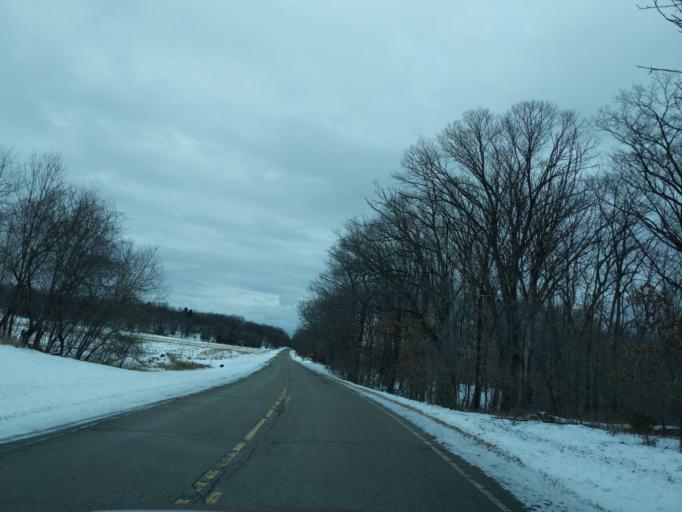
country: US
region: Wisconsin
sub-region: Marquette County
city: Montello
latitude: 43.9155
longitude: -89.3337
